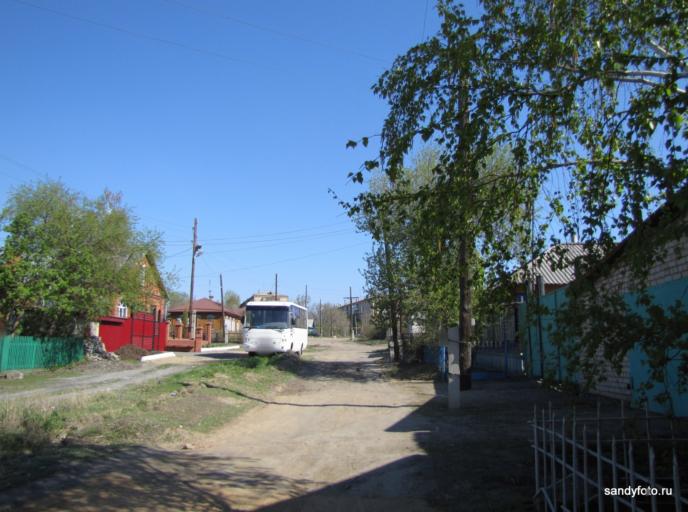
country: RU
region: Chelyabinsk
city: Troitsk
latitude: 54.1017
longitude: 61.5609
